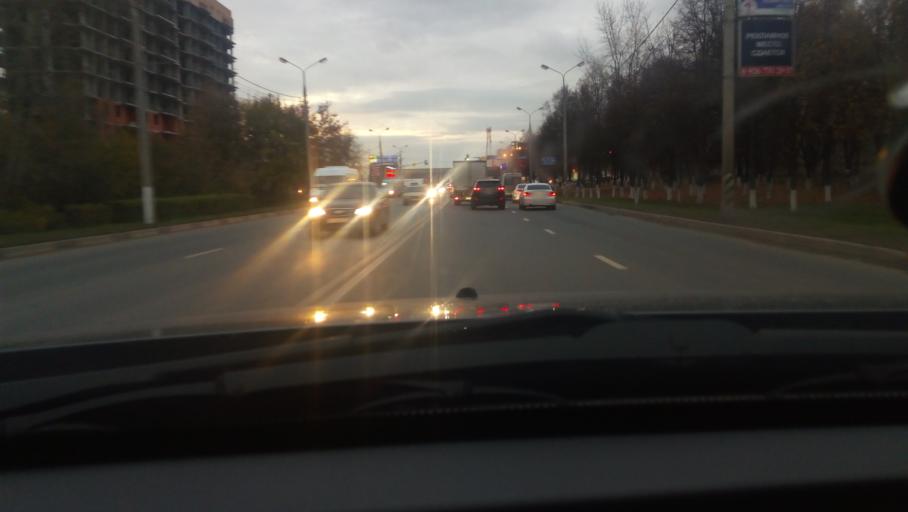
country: RU
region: Moskovskaya
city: Domodedovo
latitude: 55.4490
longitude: 37.7635
